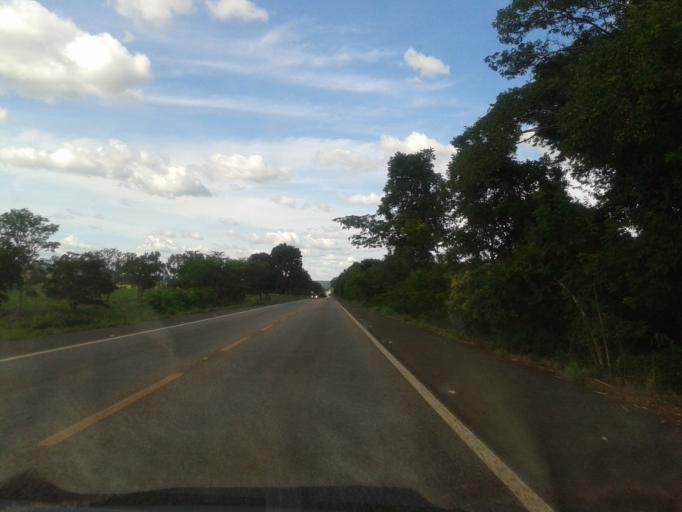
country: BR
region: Goias
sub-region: Mozarlandia
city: Mozarlandia
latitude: -15.0237
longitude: -50.5983
